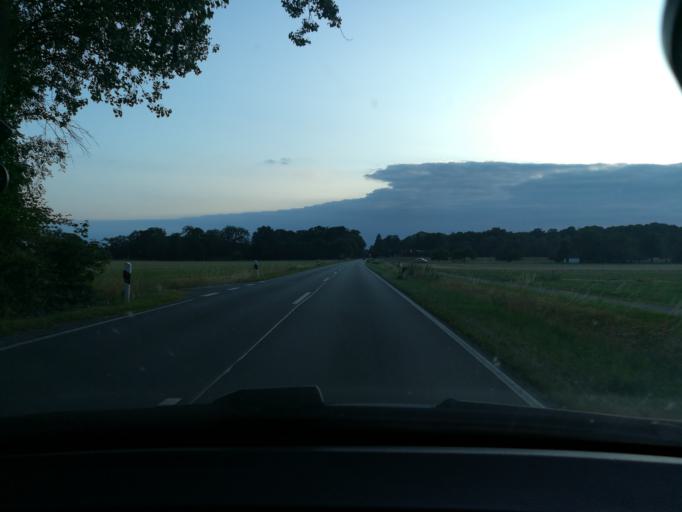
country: DE
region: North Rhine-Westphalia
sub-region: Regierungsbezirk Munster
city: Lienen
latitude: 52.1478
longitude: 7.9986
